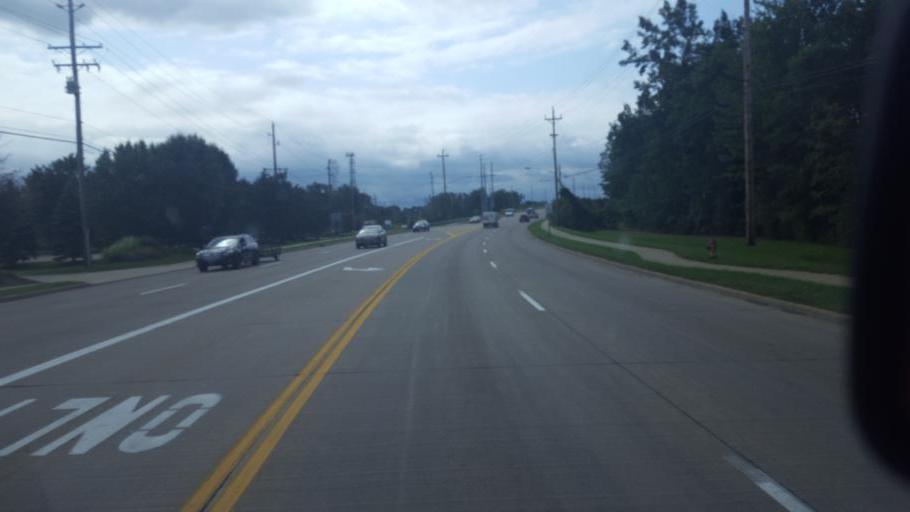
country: US
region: Ohio
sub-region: Lake County
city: Mentor
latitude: 41.7007
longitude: -81.3078
